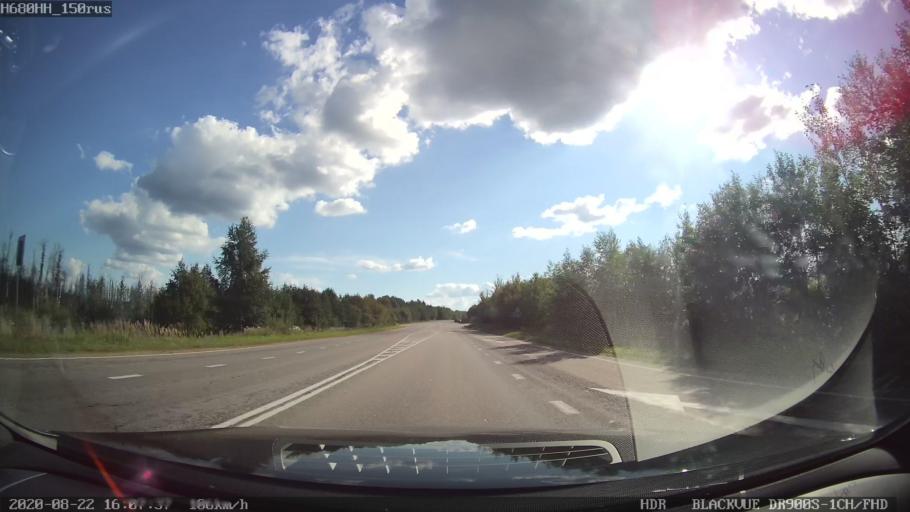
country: RU
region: Tverskaya
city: Rameshki
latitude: 57.5502
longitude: 36.3112
